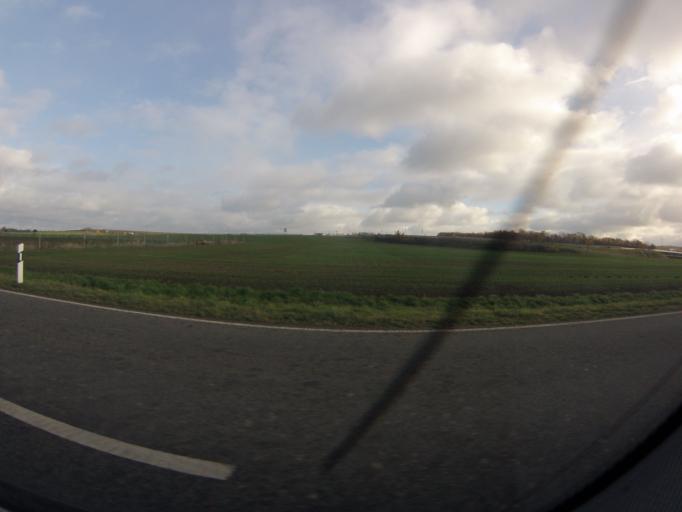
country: DE
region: Thuringia
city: Gossnitz
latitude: 50.9064
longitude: 12.4402
